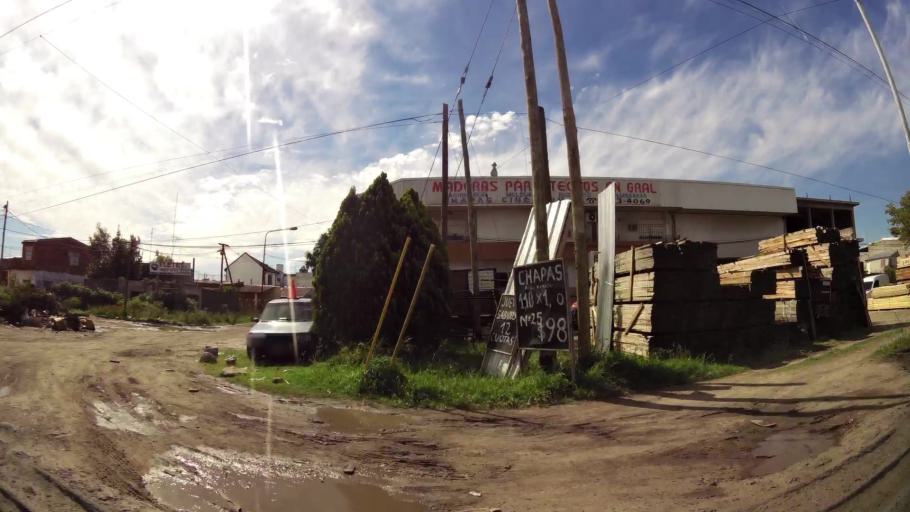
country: AR
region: Buenos Aires
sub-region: Partido de Almirante Brown
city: Adrogue
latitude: -34.7903
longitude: -58.3098
